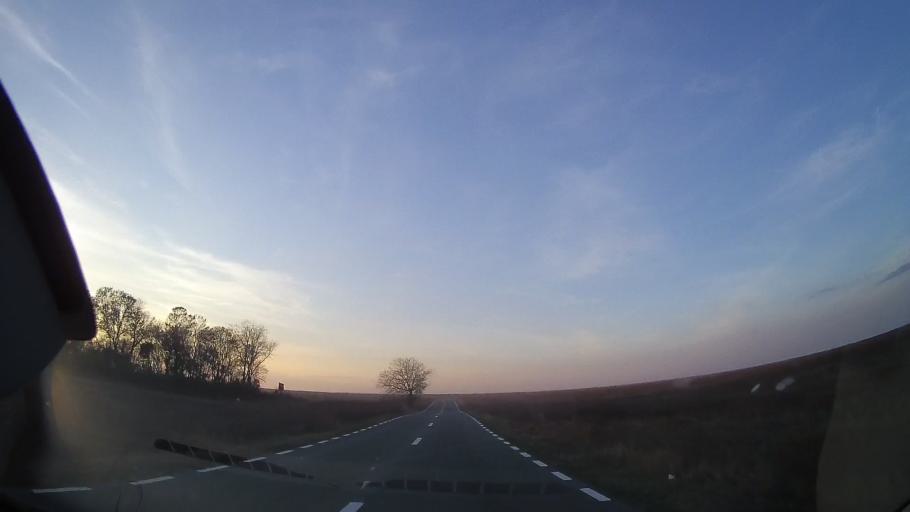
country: RO
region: Constanta
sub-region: Comuna Topraisar
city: Topraisar
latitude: 44.0131
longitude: 28.4386
